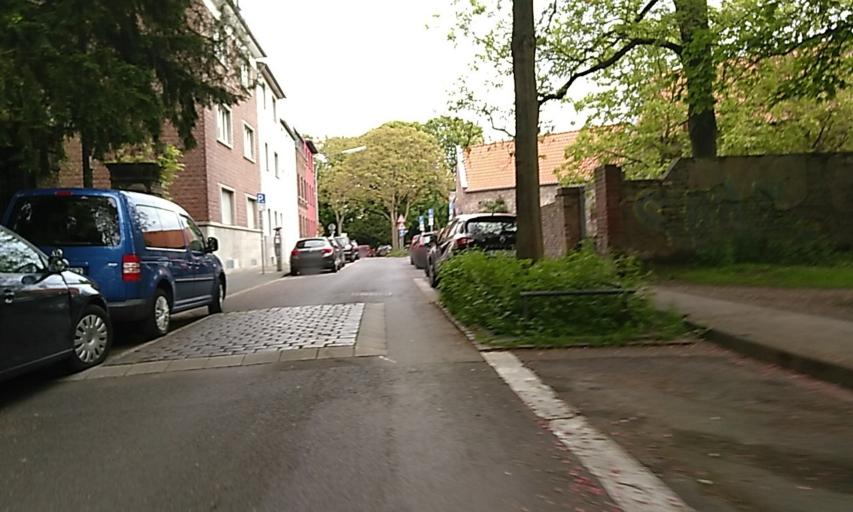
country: DE
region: North Rhine-Westphalia
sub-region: Regierungsbezirk Koln
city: Nippes
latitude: 50.9679
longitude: 6.9487
